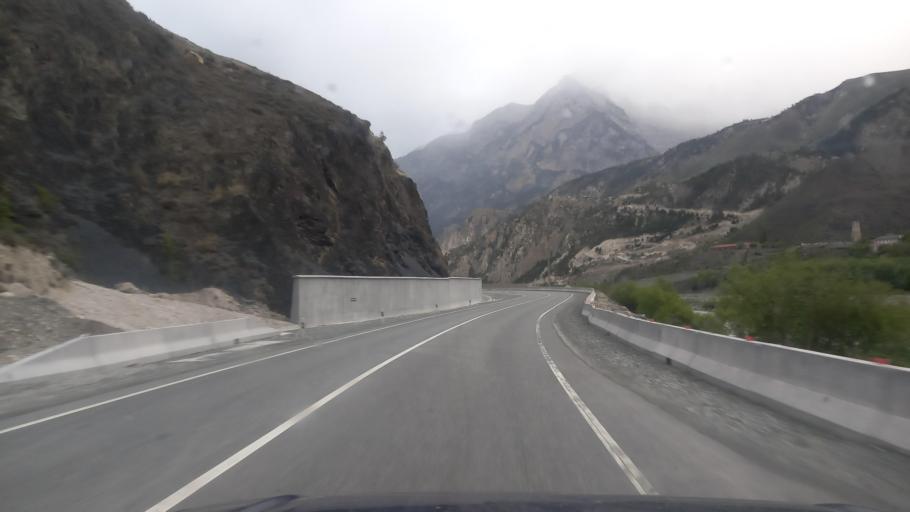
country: RU
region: North Ossetia
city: Mizur
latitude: 42.8636
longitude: 44.1463
